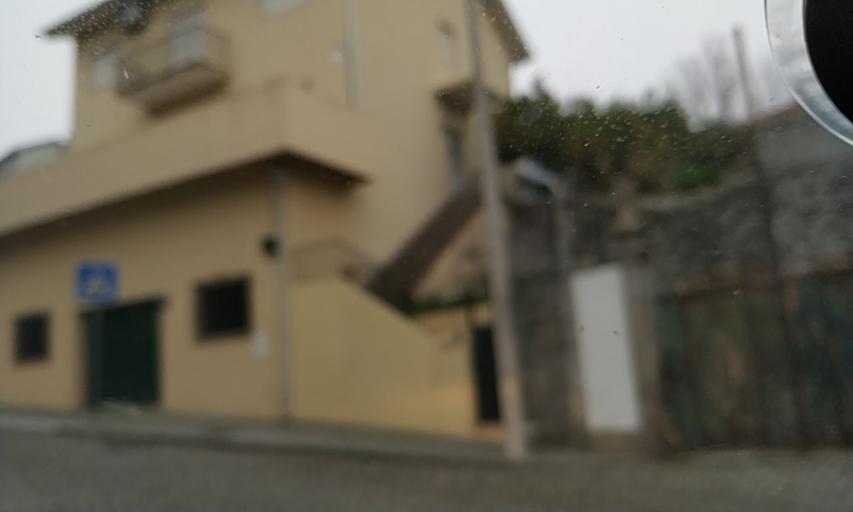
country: PT
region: Viseu
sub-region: Lamego
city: Lamego
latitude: 41.1024
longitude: -7.8088
